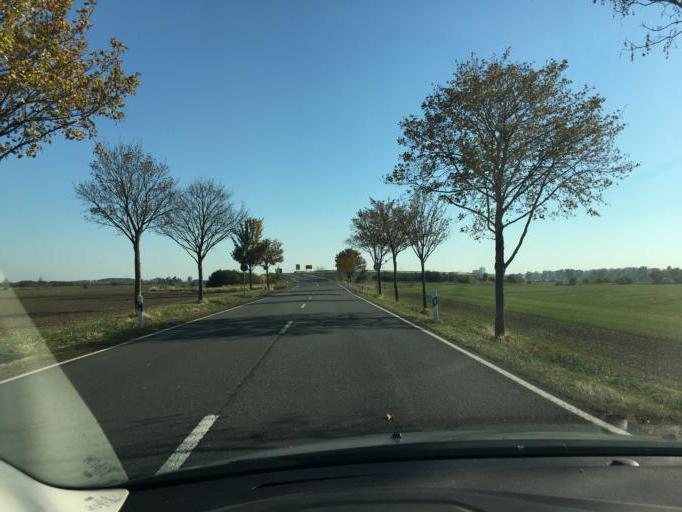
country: DE
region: Saxony-Anhalt
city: Wolmirsleben
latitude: 52.0174
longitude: 11.5025
